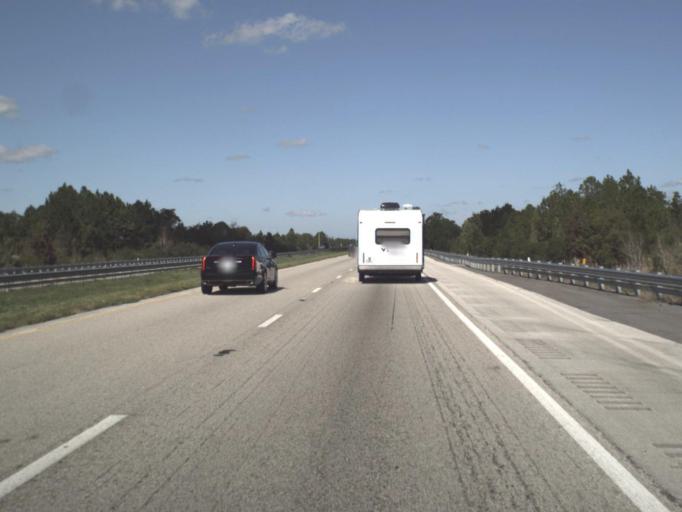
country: US
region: Florida
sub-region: Osceola County
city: Saint Cloud
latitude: 27.9424
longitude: -81.0786
